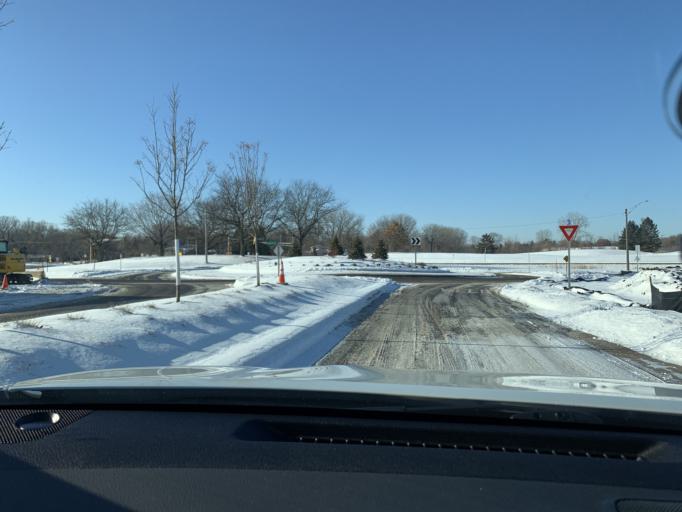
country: US
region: Minnesota
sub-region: Anoka County
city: Fridley
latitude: 45.0945
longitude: -93.2621
